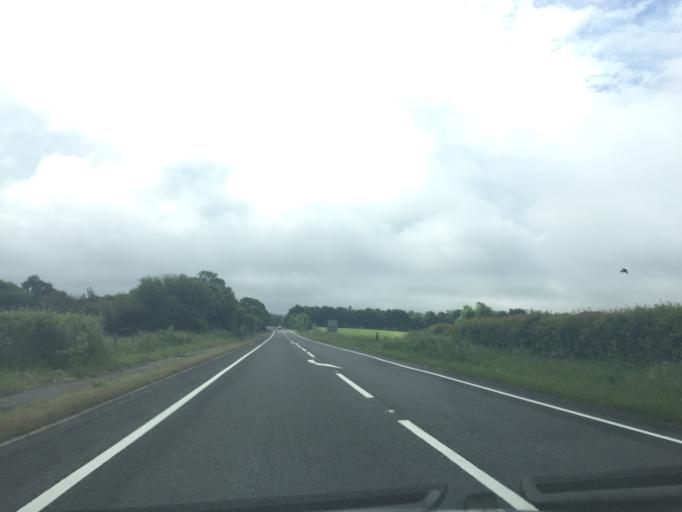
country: GB
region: England
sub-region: Dorset
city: Wareham
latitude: 50.6723
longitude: -2.1104
